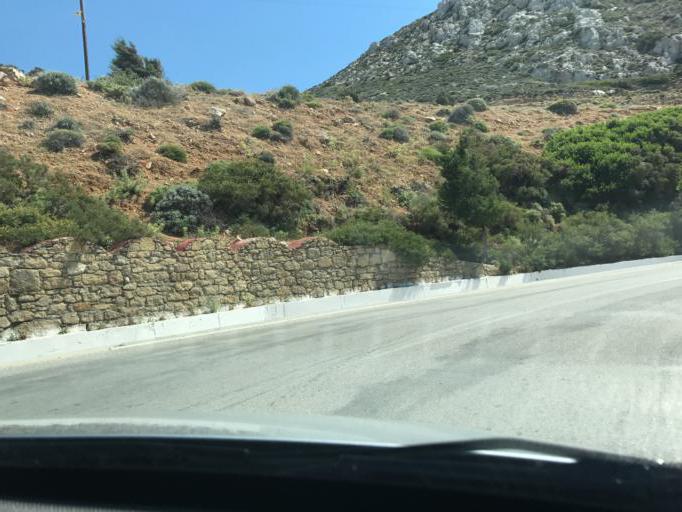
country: GR
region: South Aegean
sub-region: Nomos Dodekanisou
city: Karpathos
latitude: 35.4895
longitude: 27.1748
